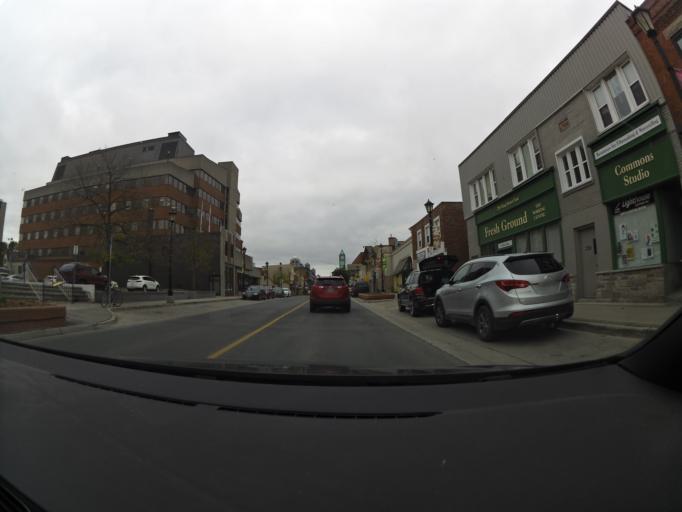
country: CA
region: Ontario
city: Kitchener
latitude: 43.4480
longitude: -80.4847
